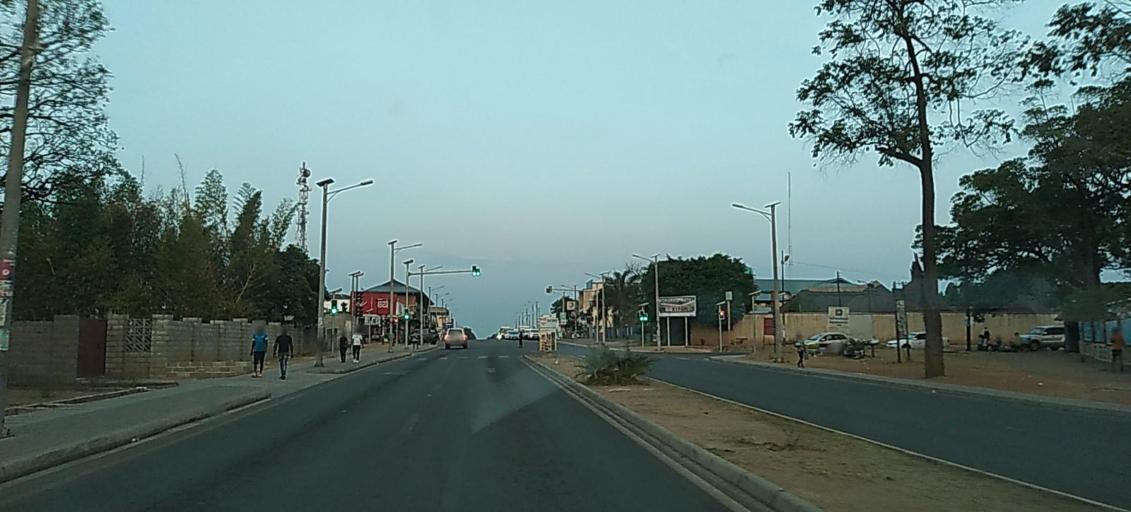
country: ZM
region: Copperbelt
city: Chingola
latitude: -12.5463
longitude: 27.8625
